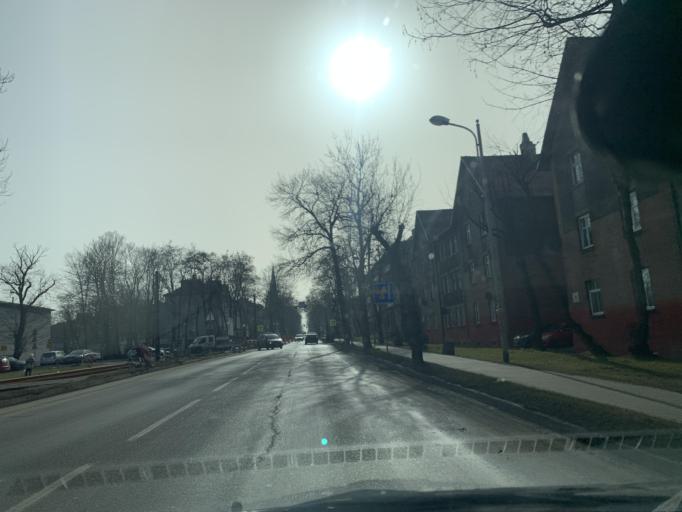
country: PL
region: Silesian Voivodeship
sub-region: Swietochlowice
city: Swietochlowice
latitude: 50.3160
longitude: 18.8876
